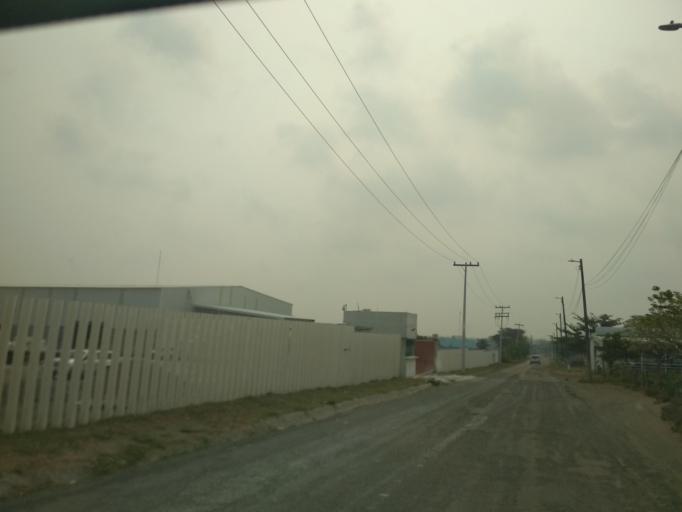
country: MX
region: Veracruz
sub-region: Veracruz
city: Delfino Victoria (Santa Fe)
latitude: 19.2098
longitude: -96.2558
